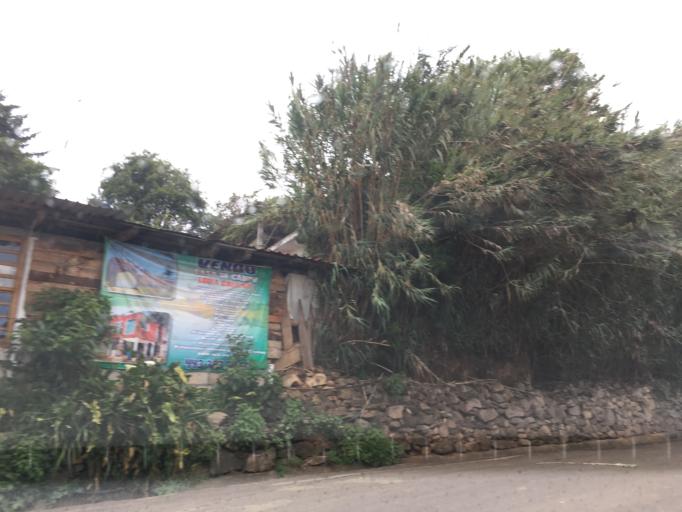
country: MX
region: Michoacan
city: Acuitzio del Canje
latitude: 19.5281
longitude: -101.2553
